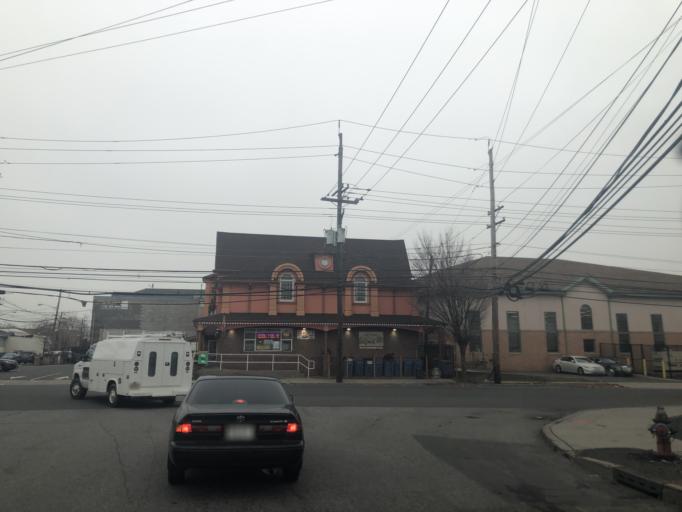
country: US
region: New Jersey
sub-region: Union County
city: Elizabeth
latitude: 40.6656
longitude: -74.1968
